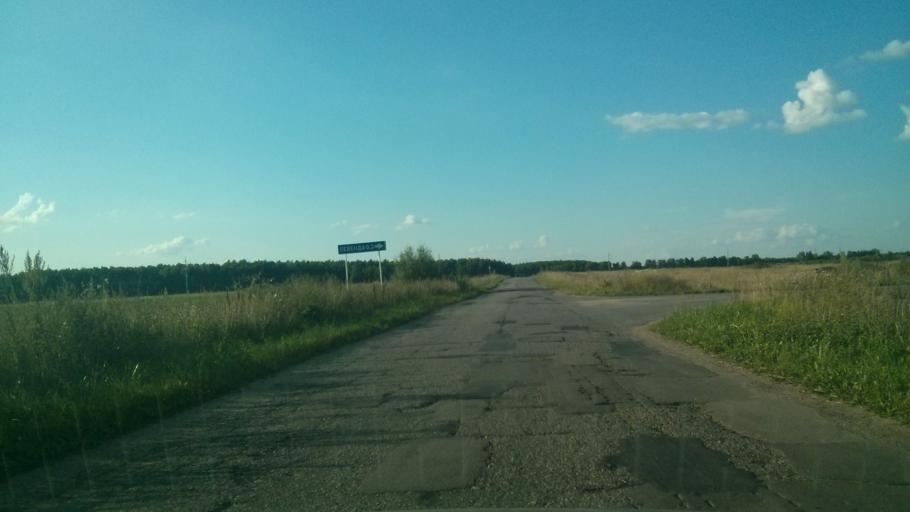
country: RU
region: Vladimir
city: Melenki
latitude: 55.3170
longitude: 41.7800
